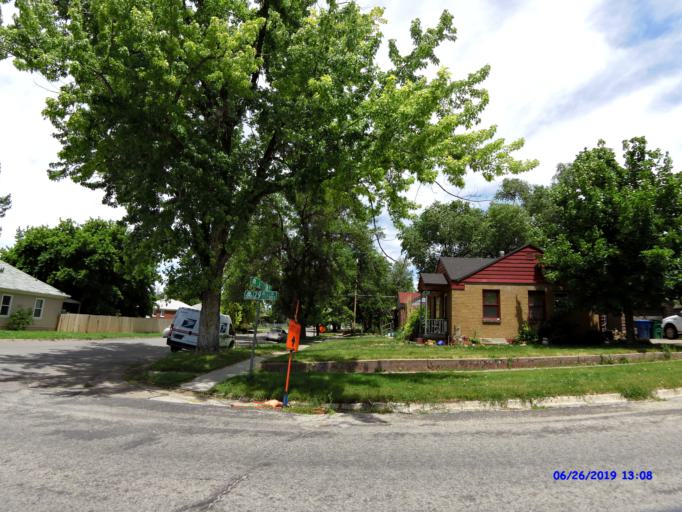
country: US
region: Utah
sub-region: Weber County
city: Ogden
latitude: 41.2122
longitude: -111.9650
